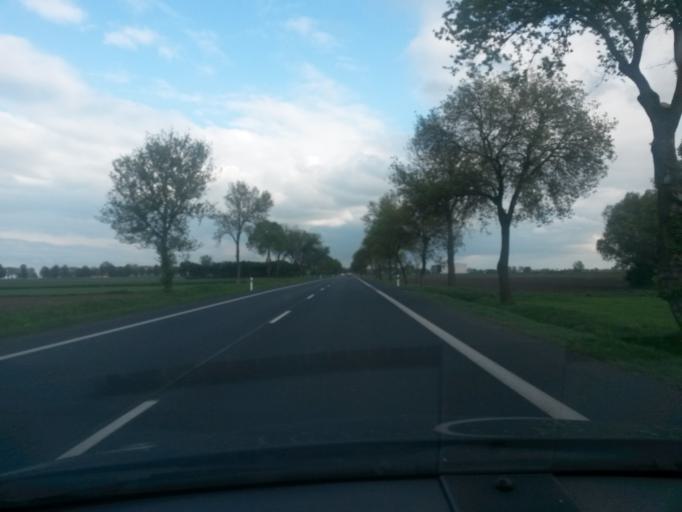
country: PL
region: Masovian Voivodeship
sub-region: Powiat plocki
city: Drobin
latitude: 52.7531
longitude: 19.9649
